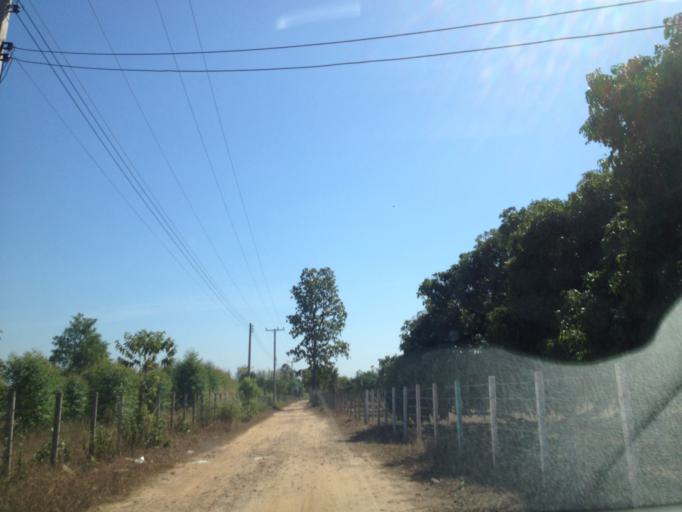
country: TH
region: Chiang Mai
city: San Pa Tong
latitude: 18.6695
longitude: 98.8715
